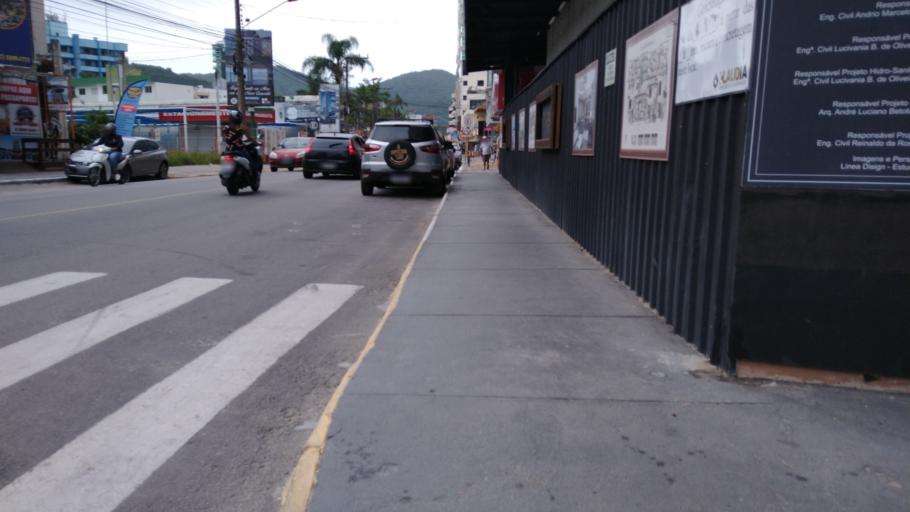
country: BR
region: Santa Catarina
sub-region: Itapema
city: Itapema
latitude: -27.0990
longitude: -48.6156
